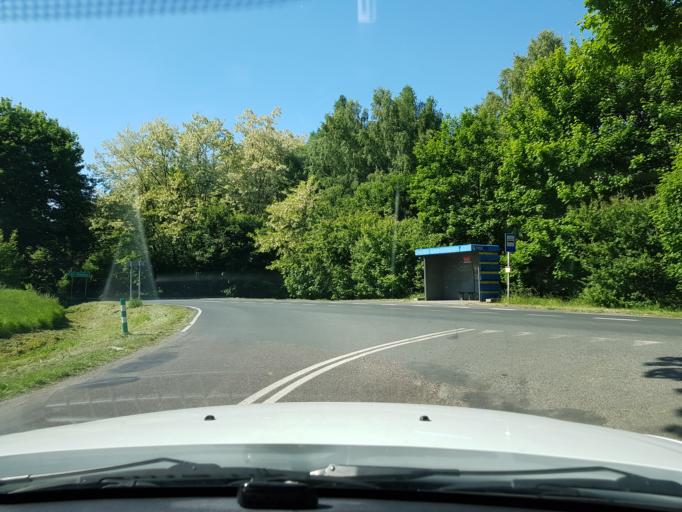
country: PL
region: West Pomeranian Voivodeship
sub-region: Powiat gryfinski
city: Gryfino
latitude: 53.1815
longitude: 14.5490
